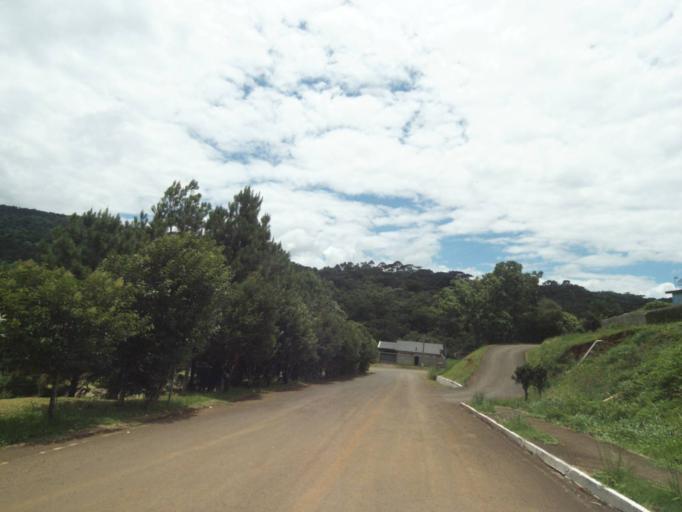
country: BR
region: Parana
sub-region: Pinhao
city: Pinhao
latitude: -26.1576
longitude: -51.5625
